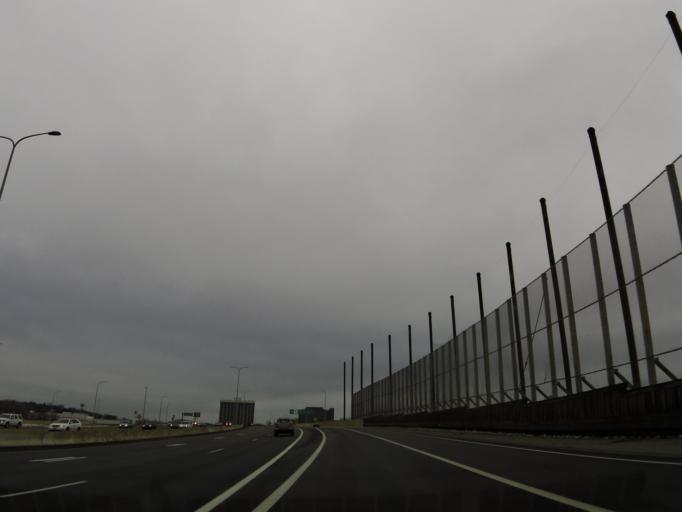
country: US
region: Minnesota
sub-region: Hennepin County
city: Saint Louis Park
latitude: 44.9740
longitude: -93.3860
